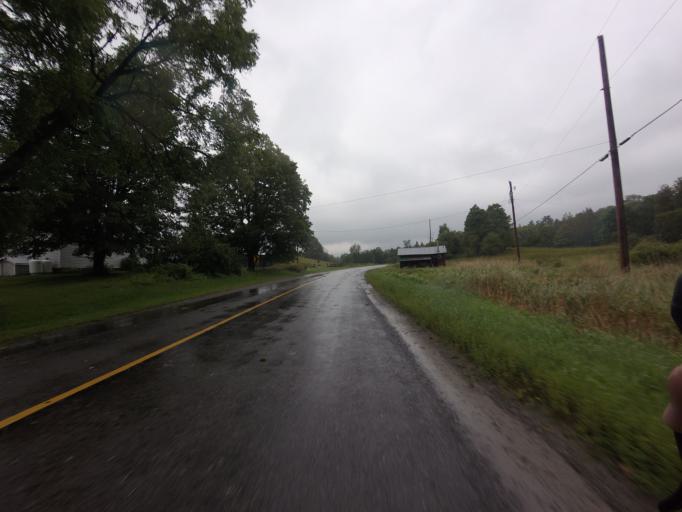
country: CA
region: Ontario
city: Perth
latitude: 45.0588
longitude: -76.5721
